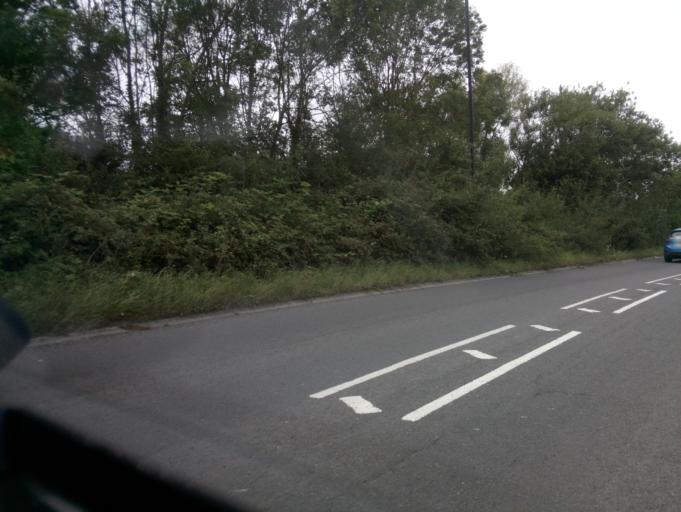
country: GB
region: England
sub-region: North Somerset
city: Kenn
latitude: 51.4243
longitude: -2.8542
